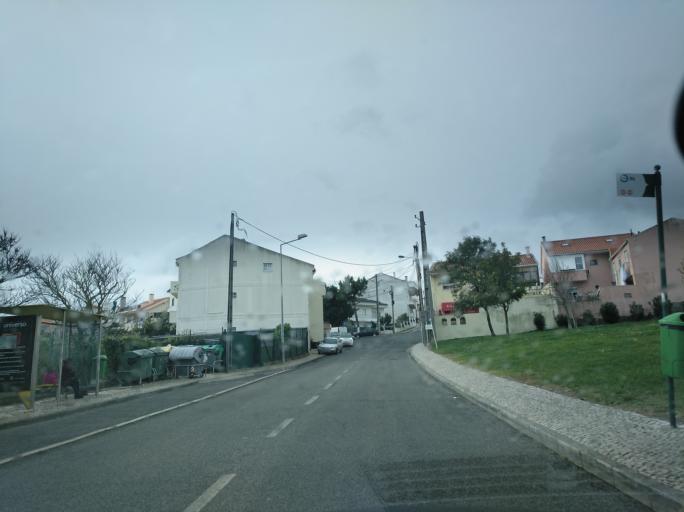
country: PT
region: Lisbon
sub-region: Odivelas
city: Famoes
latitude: 38.7930
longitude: -9.2168
